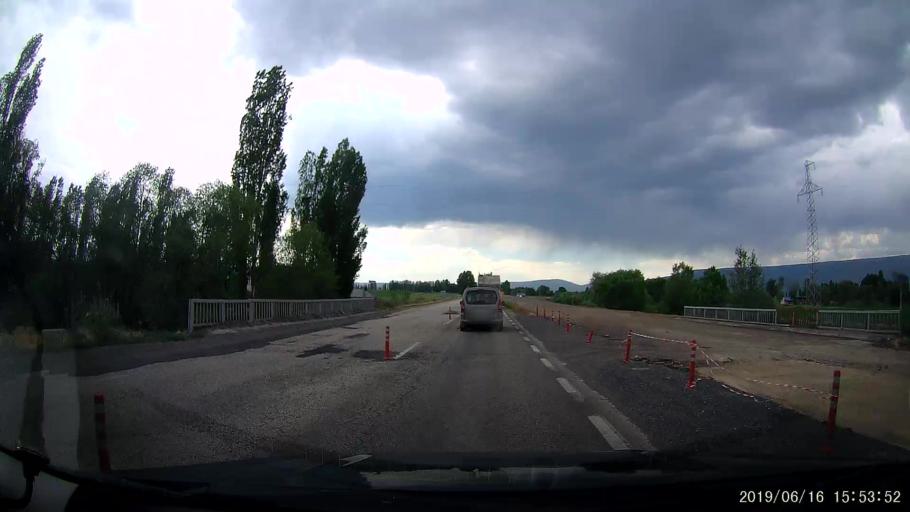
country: TR
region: Erzurum
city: Pasinler
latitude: 39.9775
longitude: 41.6412
